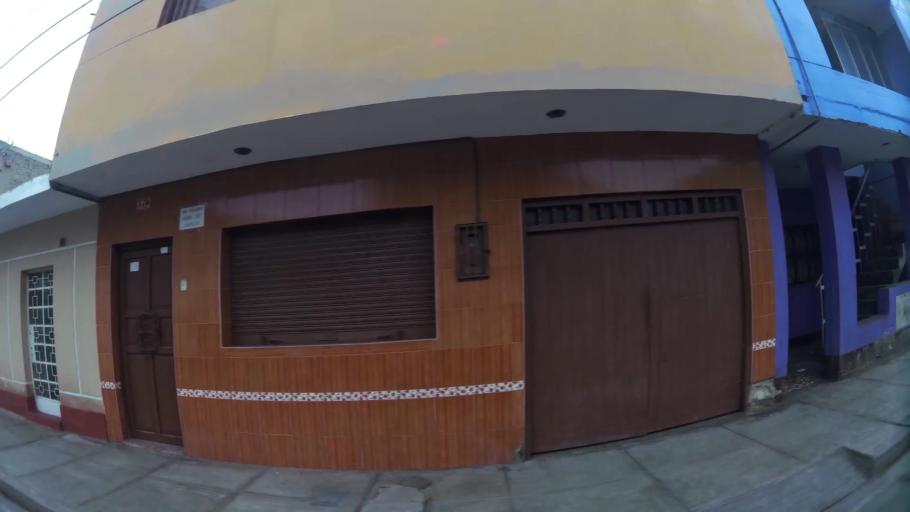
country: PE
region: Ica
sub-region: Provincia de Pisco
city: Pisco
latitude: -13.7153
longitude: -76.2050
